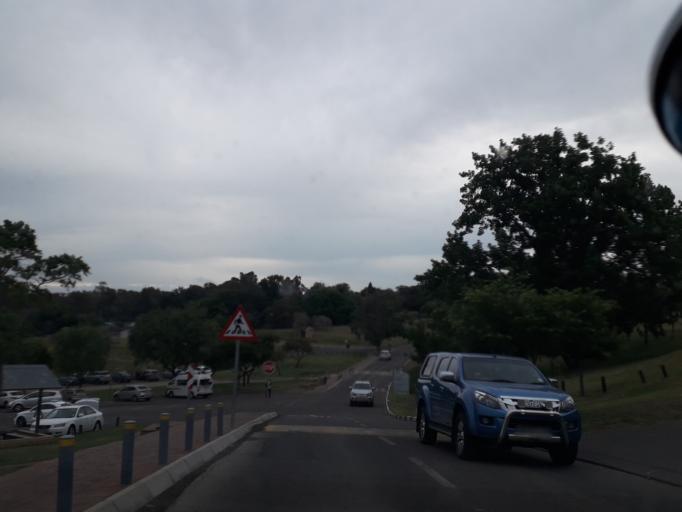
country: ZA
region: Gauteng
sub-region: City of Johannesburg Metropolitan Municipality
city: Johannesburg
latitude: -26.0829
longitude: 28.0133
